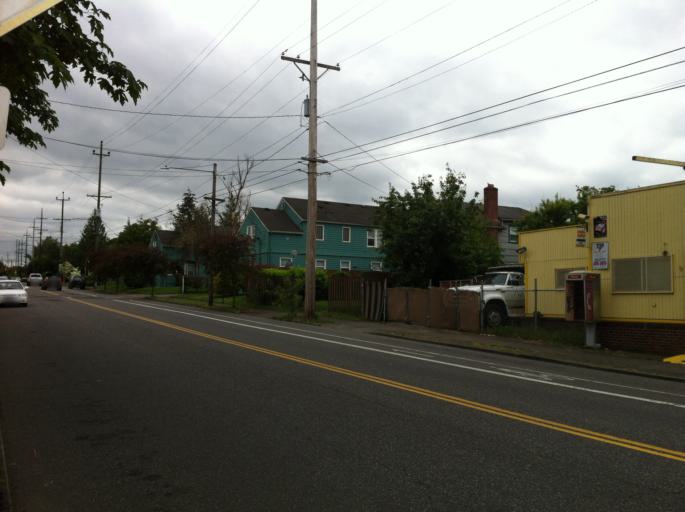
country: US
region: Oregon
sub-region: Multnomah County
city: Portland
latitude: 45.5733
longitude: -122.6687
